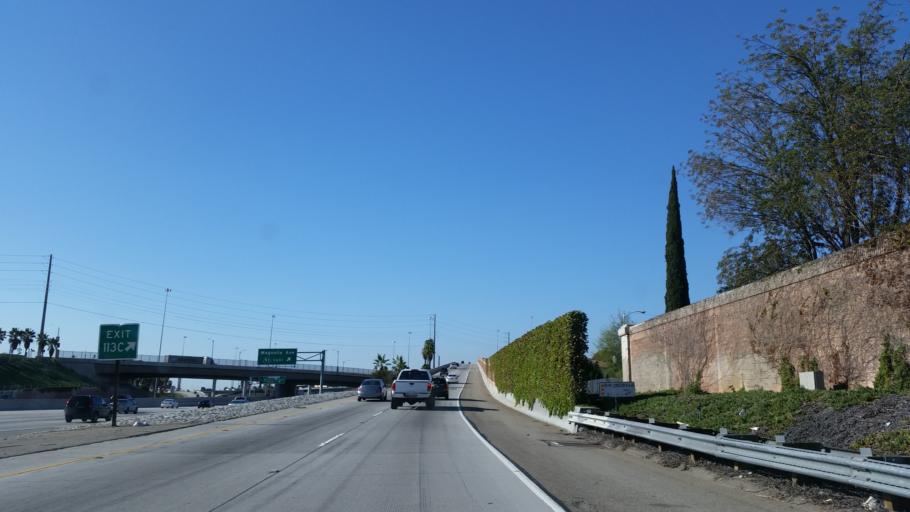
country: US
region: California
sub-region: Orange County
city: Buena Park
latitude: 33.8535
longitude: -117.9735
